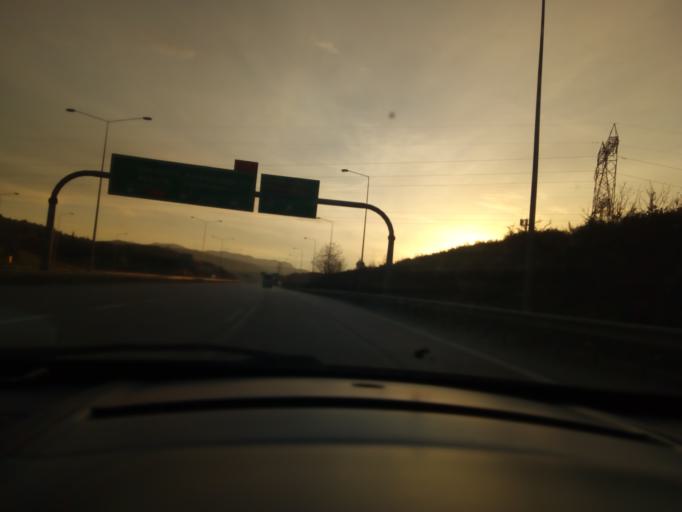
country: TR
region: Bursa
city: Demirtas
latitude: 40.2856
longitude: 29.0350
